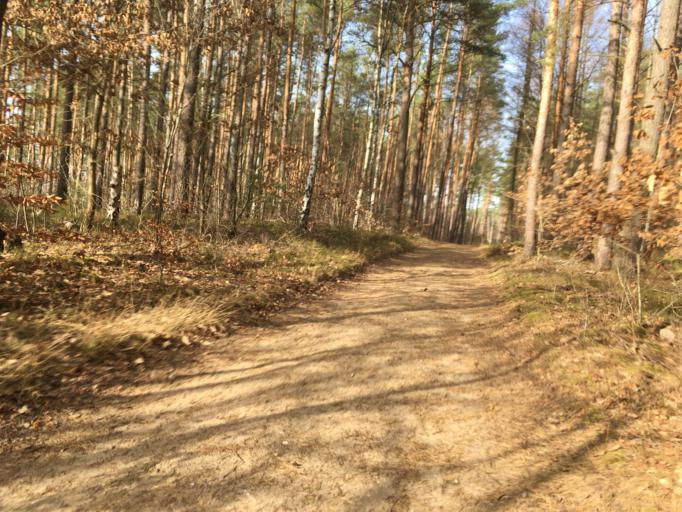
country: DE
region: Brandenburg
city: Bernau bei Berlin
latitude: 52.7047
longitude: 13.5265
